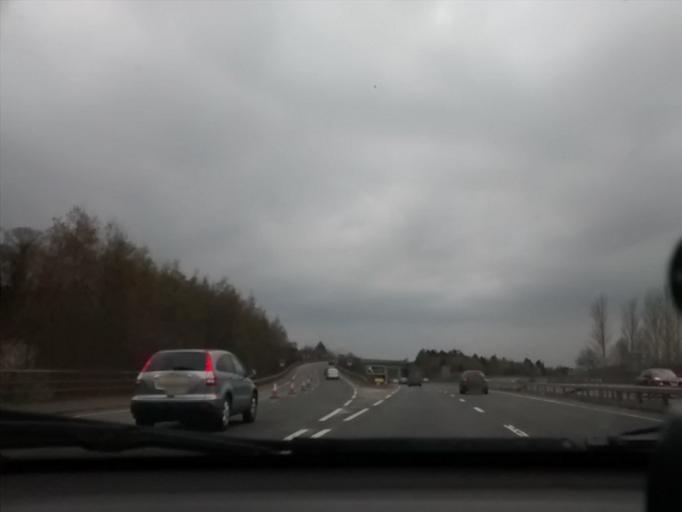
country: GB
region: England
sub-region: Cambridgeshire
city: Sawston
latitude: 52.1216
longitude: 0.2168
